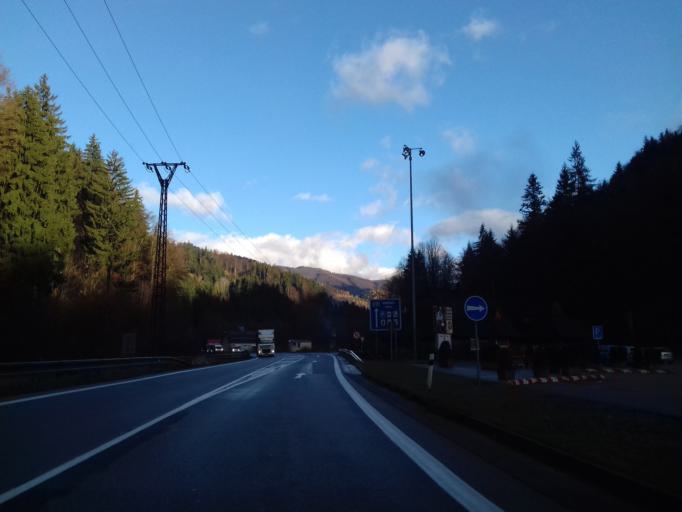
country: SK
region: Banskobystricky
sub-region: Okres Banska Bystrica
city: Banska Bystrica
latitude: 48.7935
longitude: 19.1000
